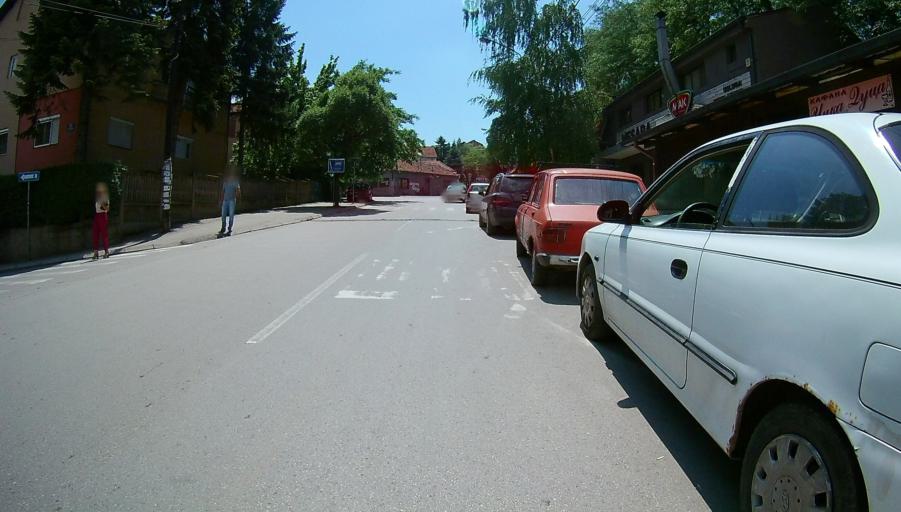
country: RS
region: Central Serbia
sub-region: Nisavski Okrug
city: Nis
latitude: 43.3100
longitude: 21.8932
